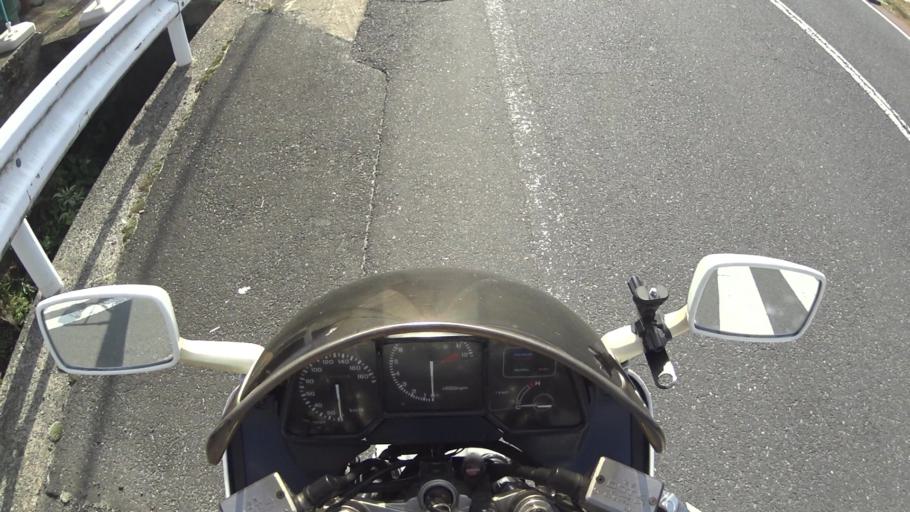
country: JP
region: Kyoto
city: Miyazu
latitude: 35.5860
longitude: 135.1018
